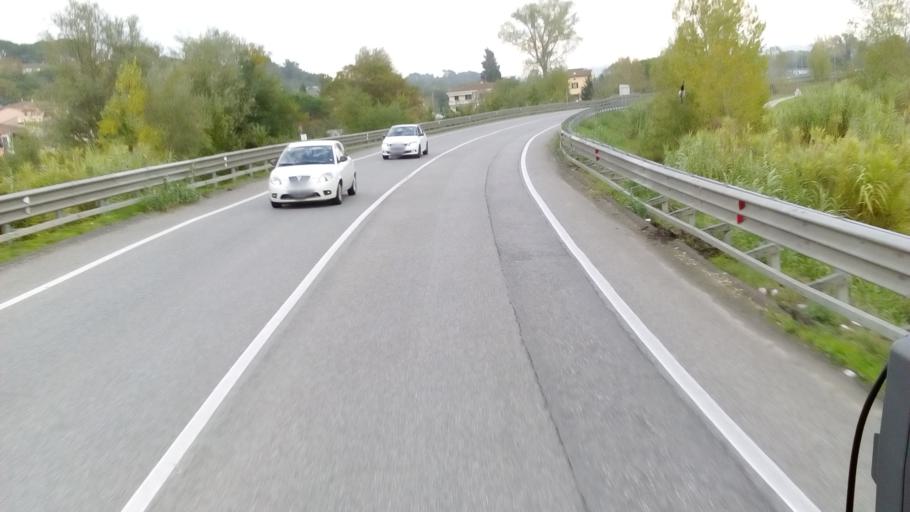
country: IT
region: Tuscany
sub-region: Province of Florence
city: Ginestra Fiorentina
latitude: 43.7090
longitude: 11.0683
